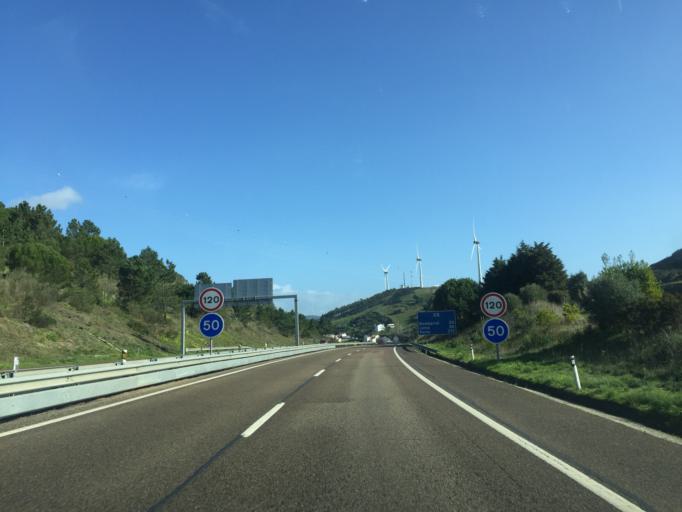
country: PT
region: Lisbon
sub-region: Torres Vedras
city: Torres Vedras
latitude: 39.0663
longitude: -9.2370
